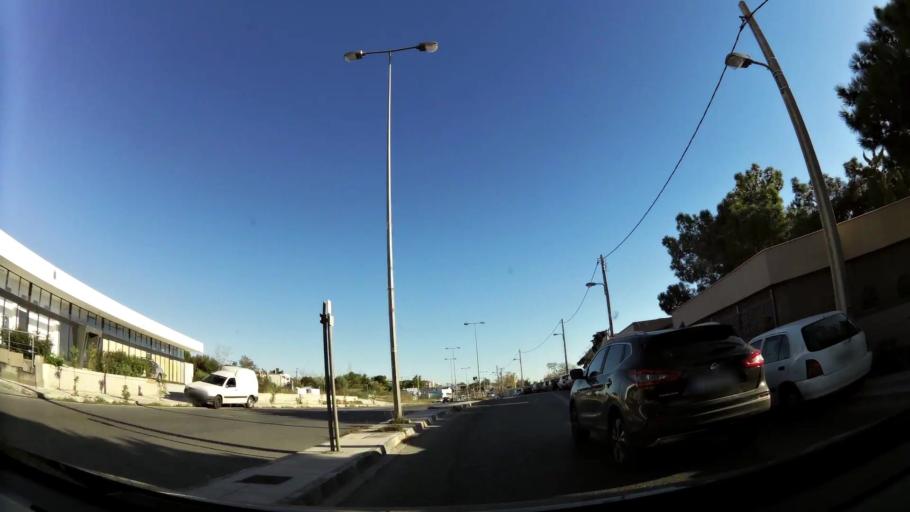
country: GR
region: Attica
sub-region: Nomarchia Anatolikis Attikis
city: Gerakas
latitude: 38.0400
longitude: 23.8500
